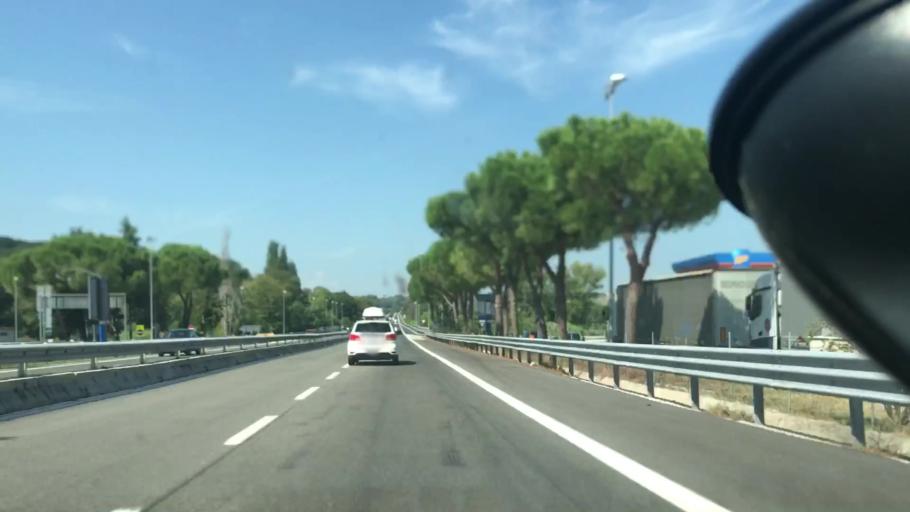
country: IT
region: Abruzzo
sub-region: Provincia di Chieti
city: Torino di Sangro
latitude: 42.2002
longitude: 14.5627
